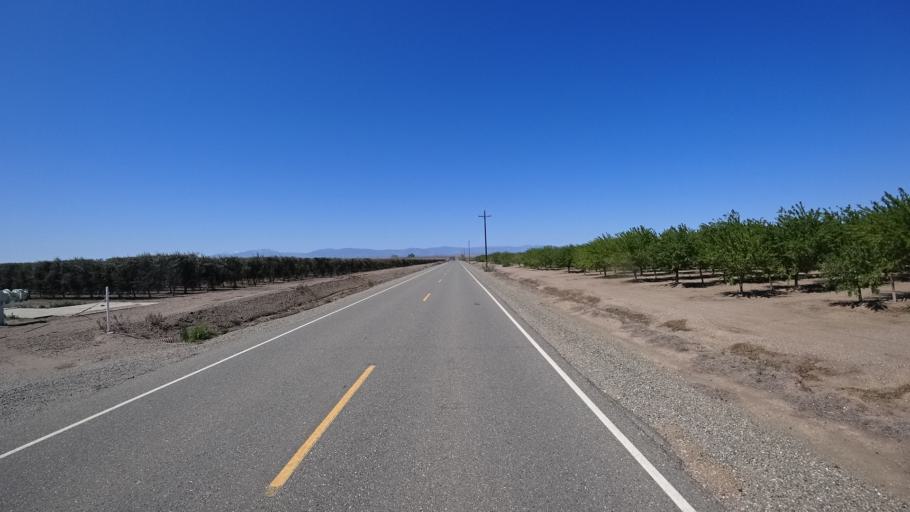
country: US
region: California
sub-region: Glenn County
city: Willows
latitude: 39.6246
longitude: -122.2416
